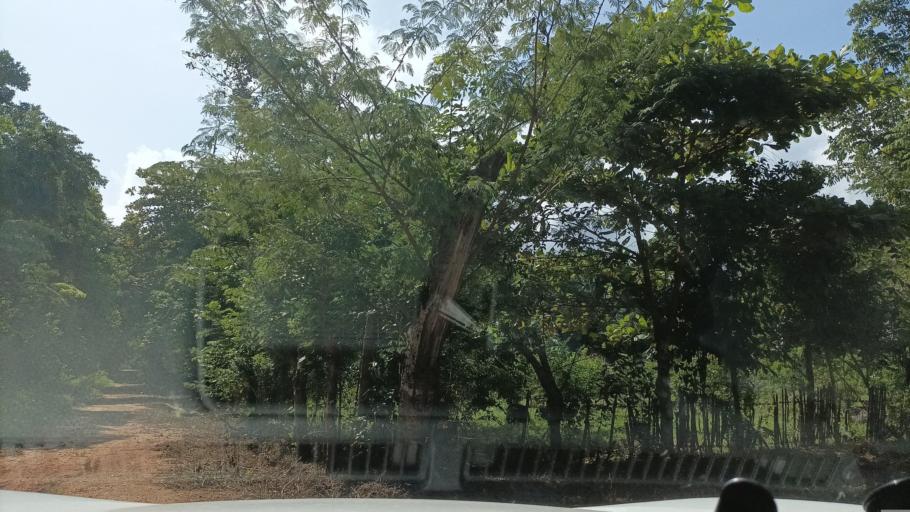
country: MX
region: Veracruz
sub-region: Chinameca
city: Chacalapa
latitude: 18.0804
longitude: -94.6683
